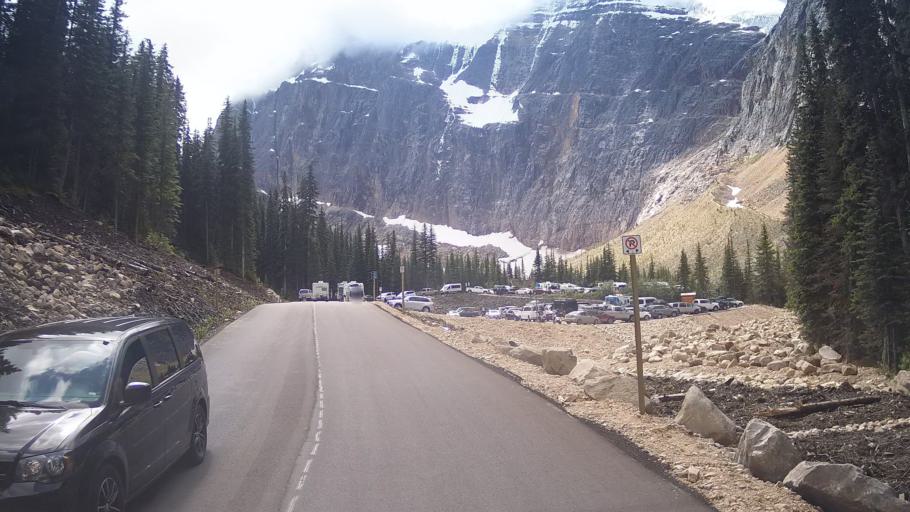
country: CA
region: Alberta
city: Jasper Park Lodge
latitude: 52.6889
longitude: -118.0560
